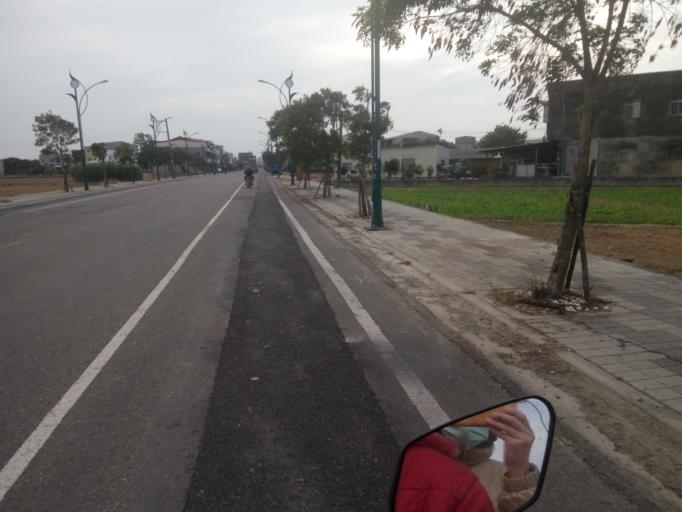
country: TW
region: Taiwan
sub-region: Chiayi
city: Taibao
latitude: 23.4933
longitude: 120.3564
